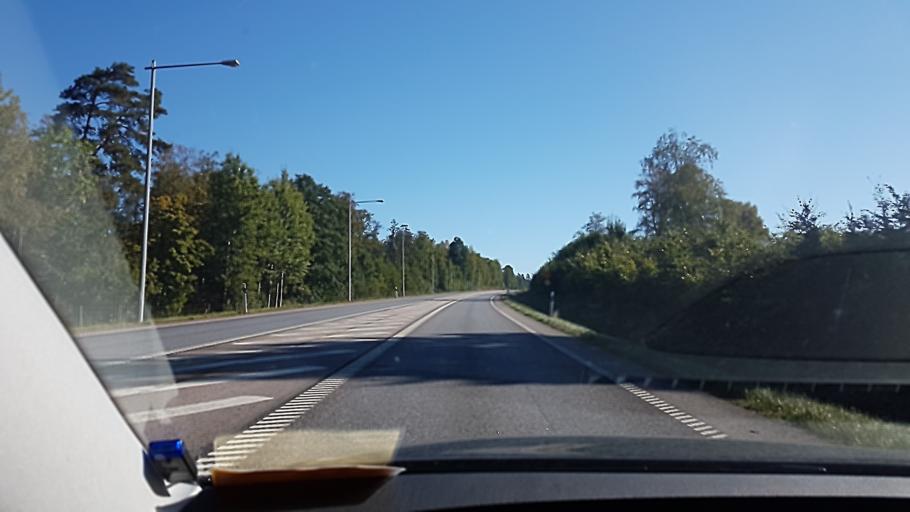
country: SE
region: Kronoberg
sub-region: Vaxjo Kommun
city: Vaexjoe
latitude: 56.8828
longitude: 14.8433
